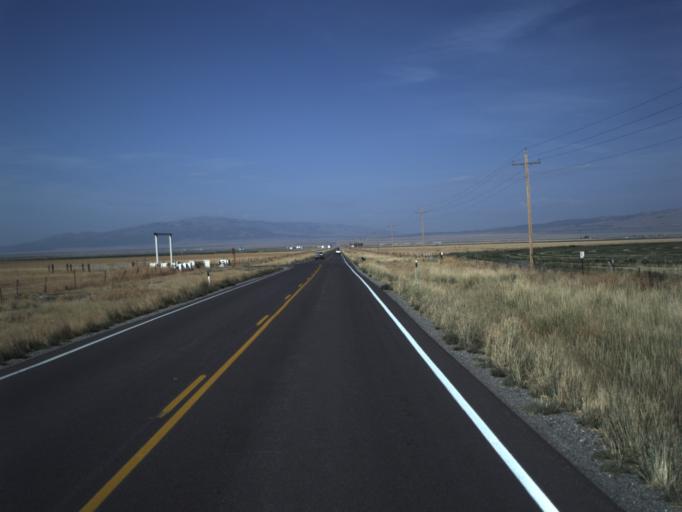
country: US
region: Idaho
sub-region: Oneida County
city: Malad City
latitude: 41.9673
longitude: -112.8367
